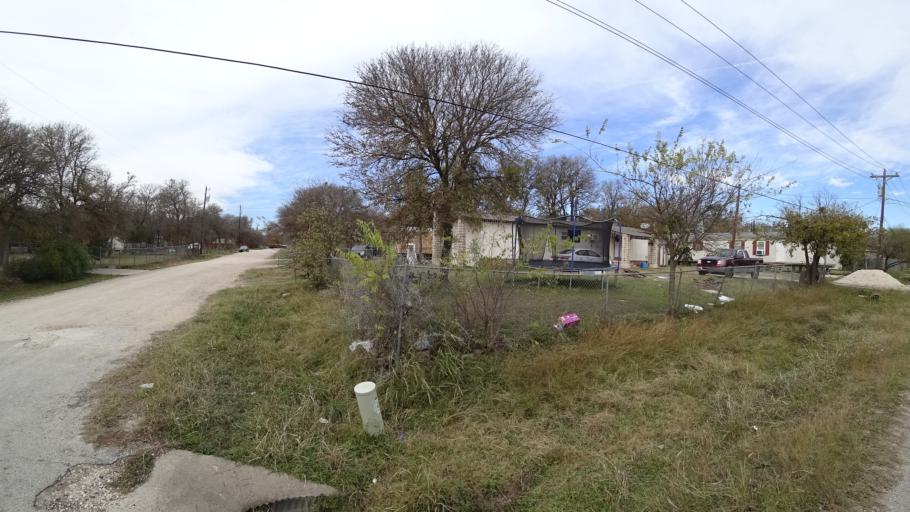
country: US
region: Texas
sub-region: Travis County
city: Garfield
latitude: 30.1330
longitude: -97.5648
